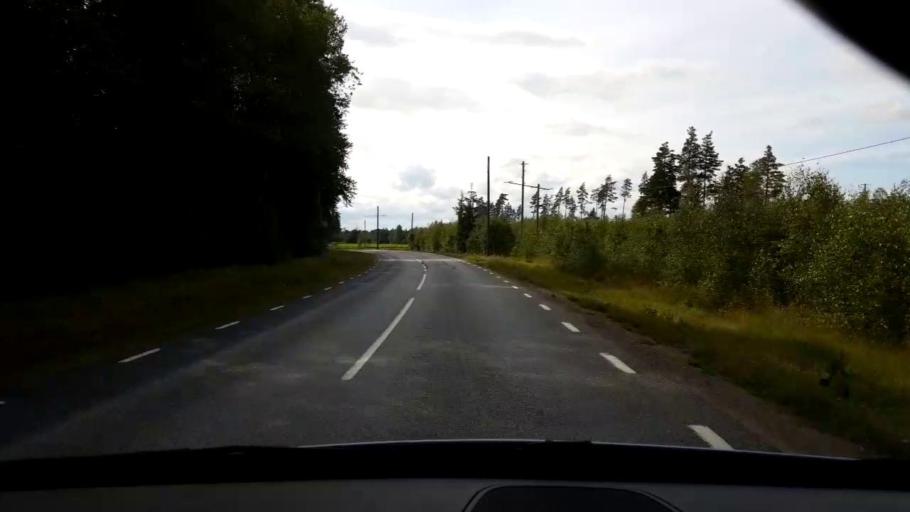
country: SE
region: Joenkoeping
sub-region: Vetlanda Kommun
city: Landsbro
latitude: 57.3793
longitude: 14.9952
